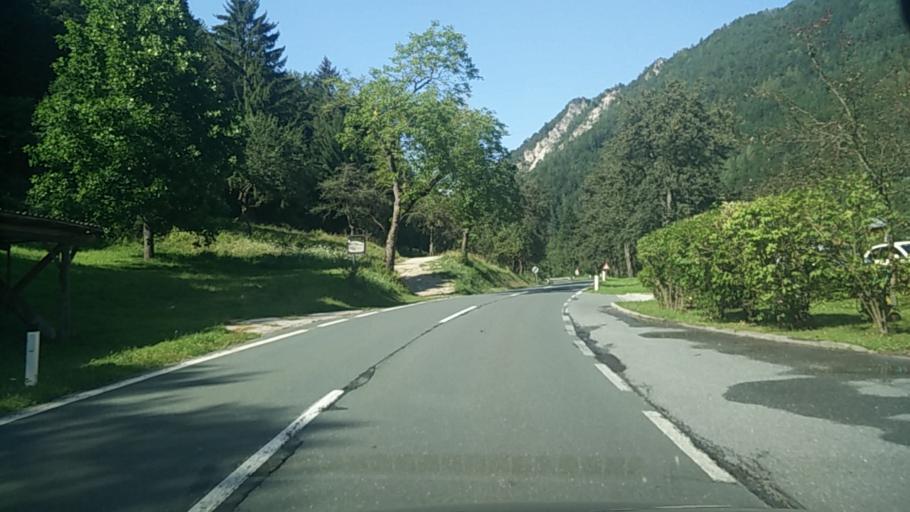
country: AT
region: Carinthia
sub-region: Politischer Bezirk Volkermarkt
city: Bad Eisenkappel
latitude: 46.5003
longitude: 14.5822
